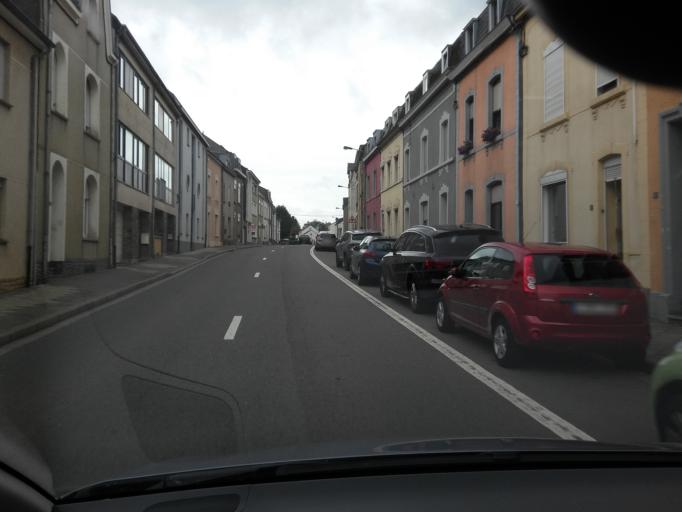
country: BE
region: Wallonia
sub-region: Province du Luxembourg
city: Arlon
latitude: 49.6750
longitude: 5.8136
